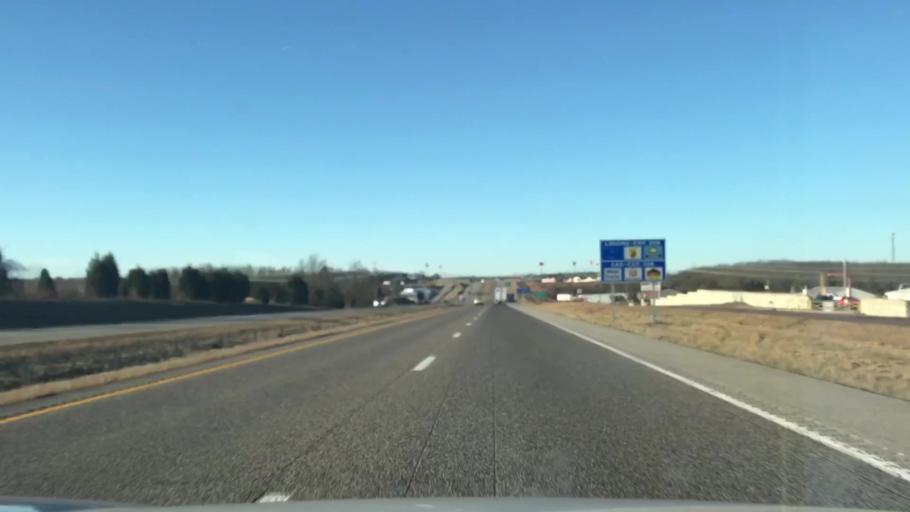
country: US
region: Missouri
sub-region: Crawford County
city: Cuba
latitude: 38.0800
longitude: -91.3945
